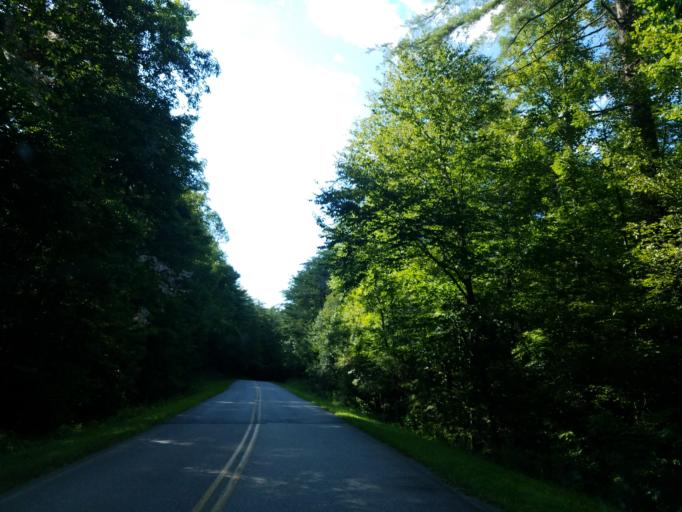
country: US
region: Georgia
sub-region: Fannin County
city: Blue Ridge
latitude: 34.7229
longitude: -84.2358
